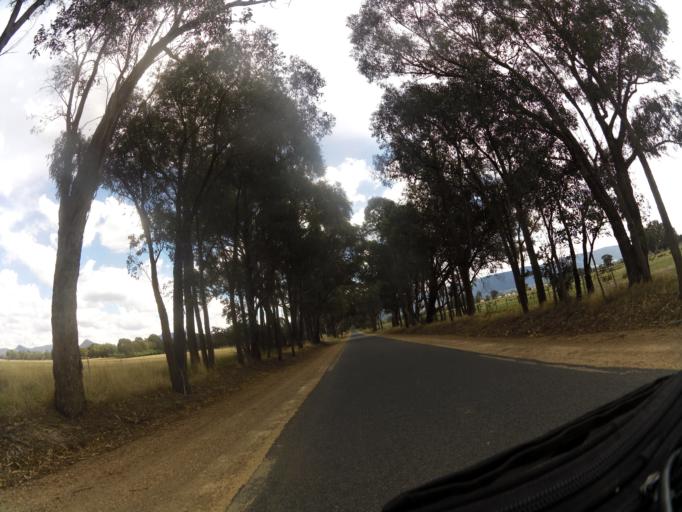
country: AU
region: Victoria
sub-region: Benalla
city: Benalla
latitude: -36.7491
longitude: 145.9935
